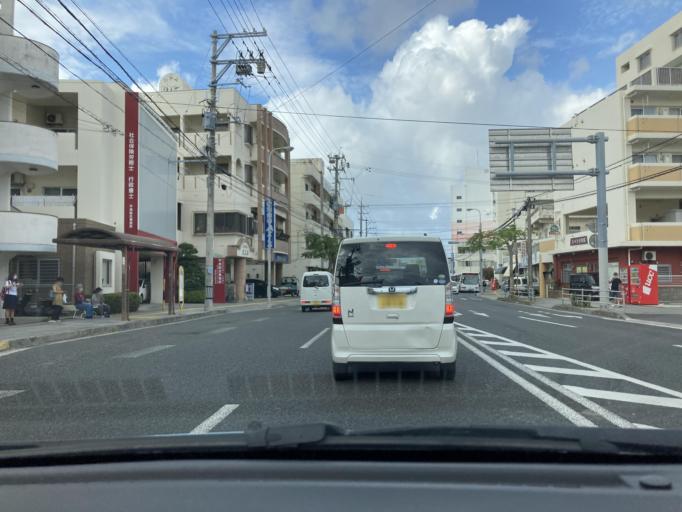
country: JP
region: Okinawa
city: Tomigusuku
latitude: 26.1946
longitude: 127.6761
